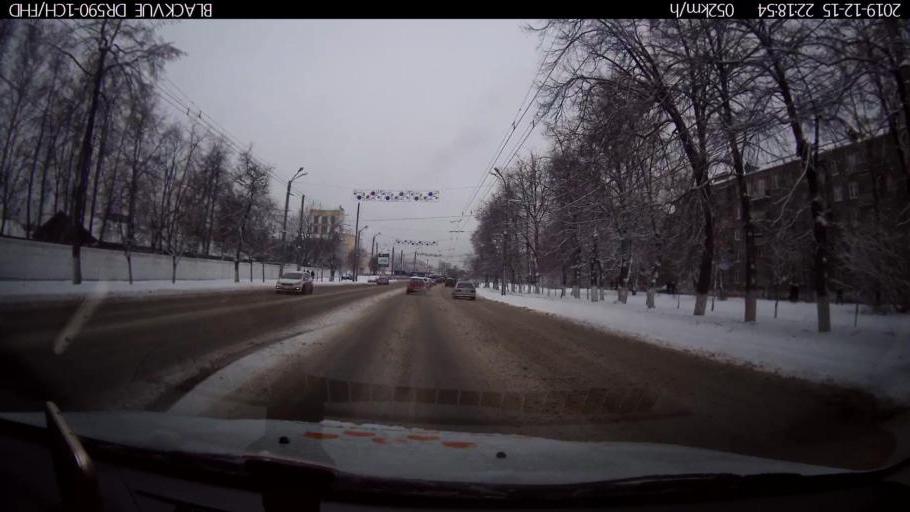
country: RU
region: Nizjnij Novgorod
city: Nizhniy Novgorod
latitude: 56.3240
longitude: 43.9167
